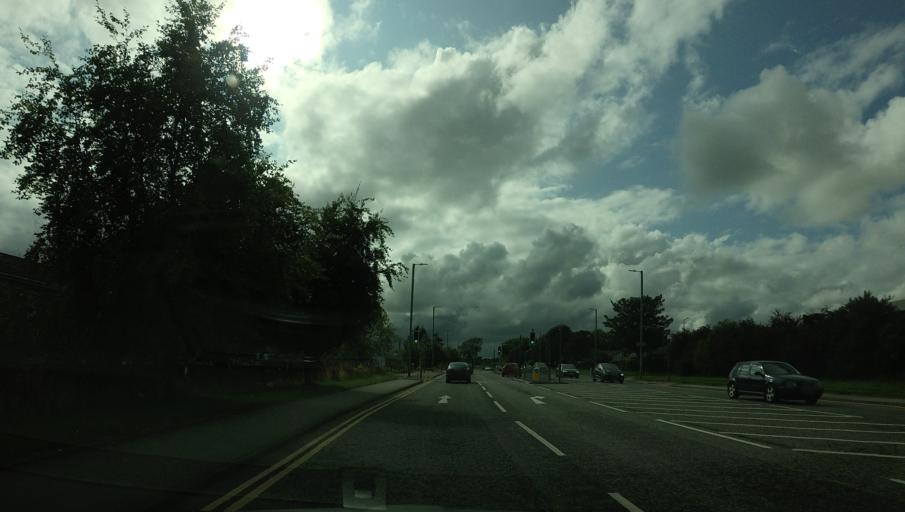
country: GB
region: Scotland
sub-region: Aberdeen City
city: Cults
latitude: 57.1506
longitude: -2.1790
